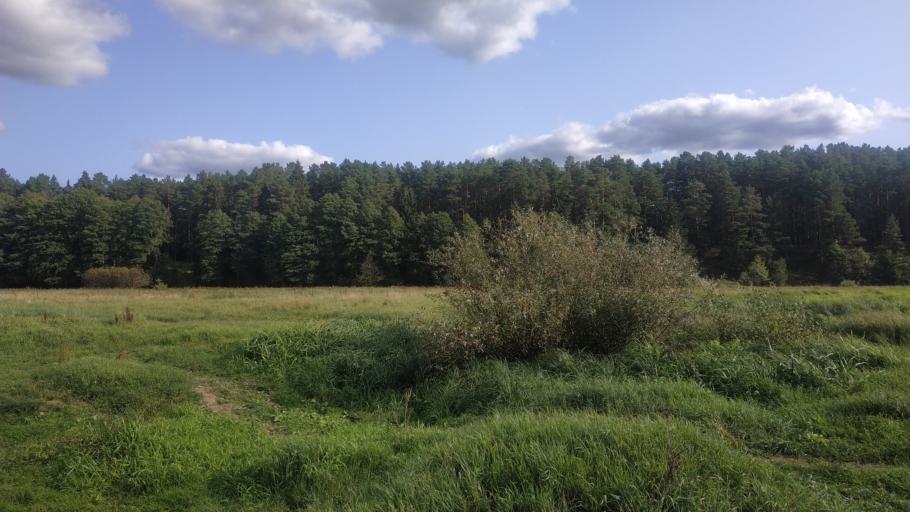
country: RU
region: Brjansk
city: Zhukovka
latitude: 53.5283
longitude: 33.6899
